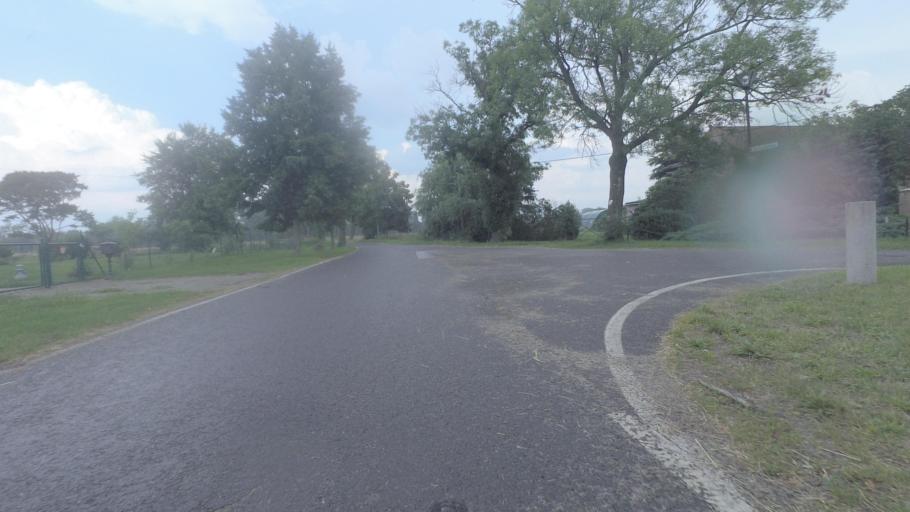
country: DE
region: Brandenburg
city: Trebbin
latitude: 52.2797
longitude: 13.1615
